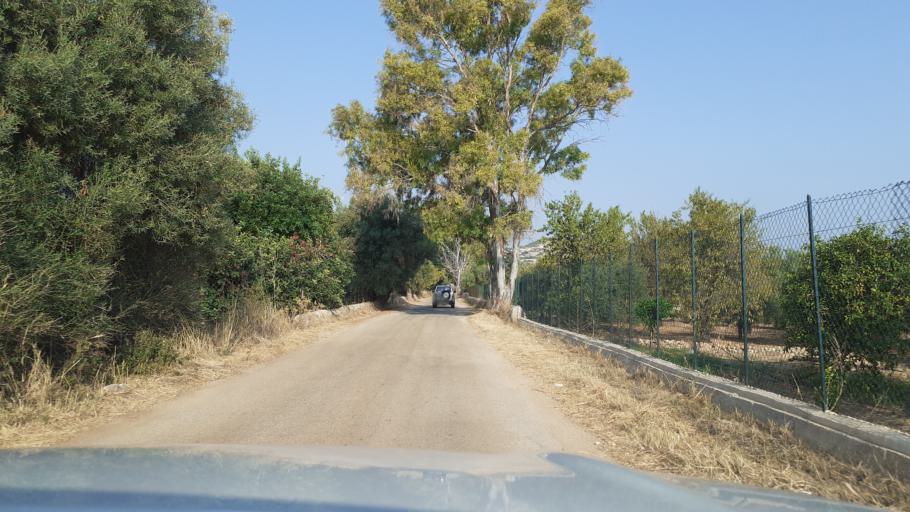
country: IT
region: Sicily
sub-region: Provincia di Siracusa
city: Cassibile
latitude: 36.9750
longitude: 15.1864
